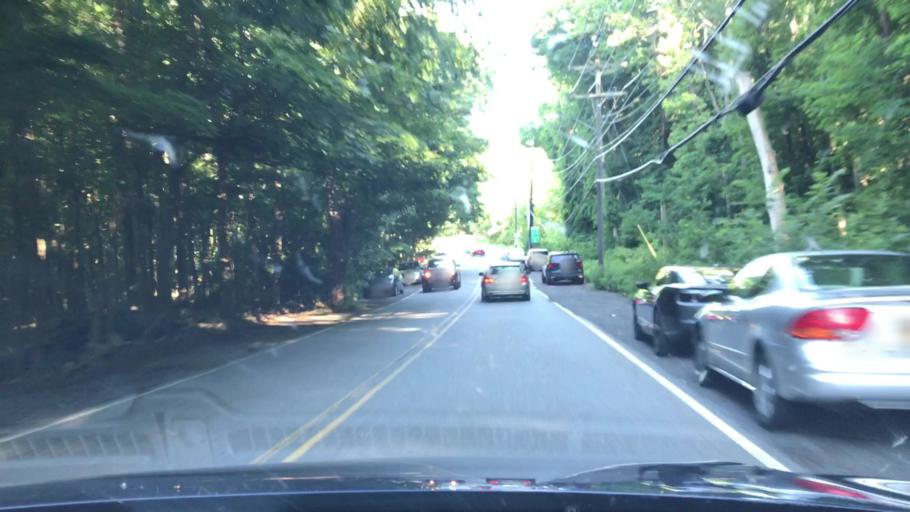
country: US
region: New York
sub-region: Westchester County
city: Heritage Hills
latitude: 41.3516
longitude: -73.6665
